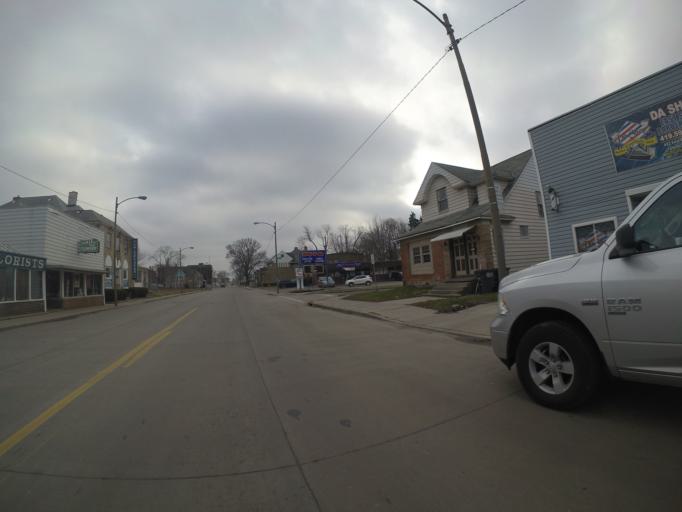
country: US
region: Ohio
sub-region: Lucas County
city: Oregon
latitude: 41.6429
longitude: -83.5159
